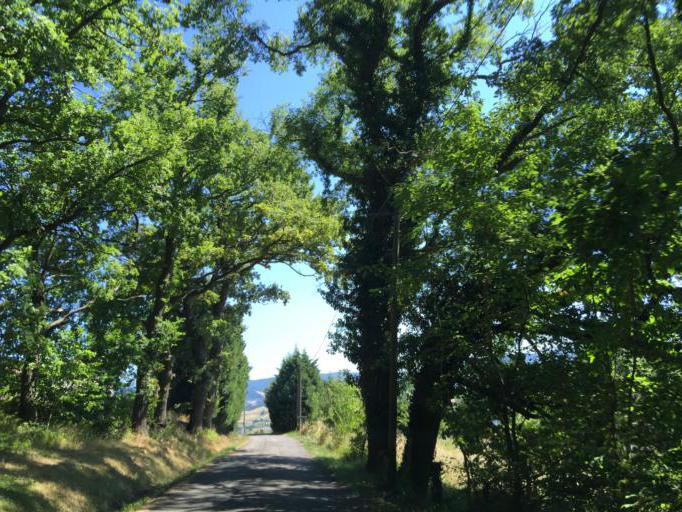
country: FR
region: Rhone-Alpes
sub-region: Departement de la Loire
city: Saint-Jean-Bonnefonds
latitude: 45.4652
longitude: 4.4604
